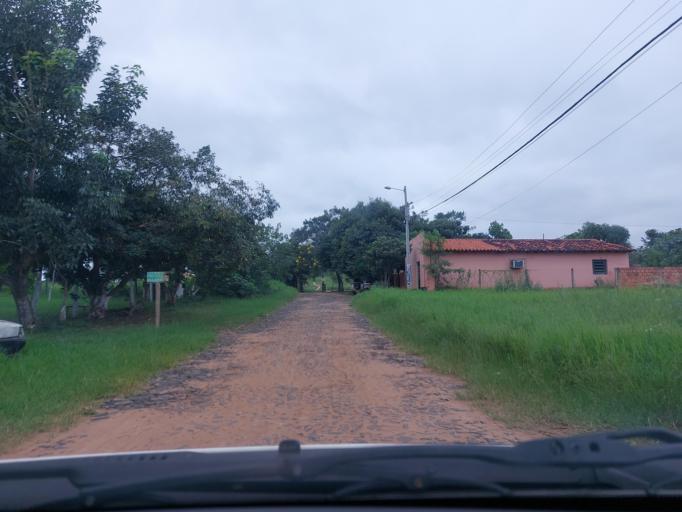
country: PY
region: San Pedro
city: Guayaybi
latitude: -24.6679
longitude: -56.4342
